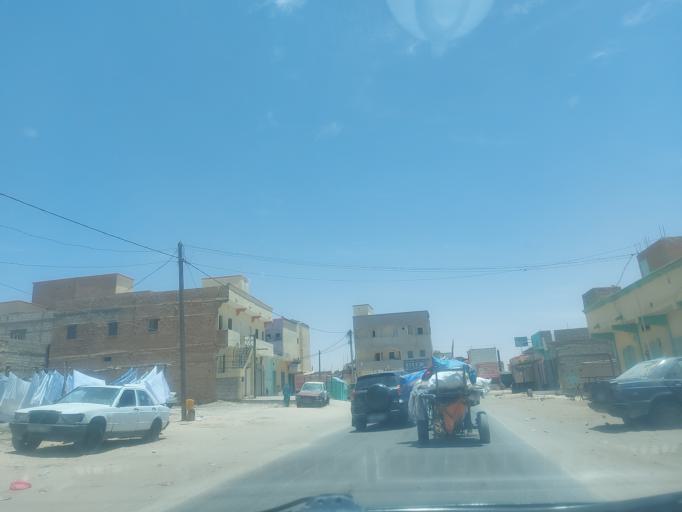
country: MR
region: Nouakchott
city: Nouakchott
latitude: 18.0680
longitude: -15.9439
